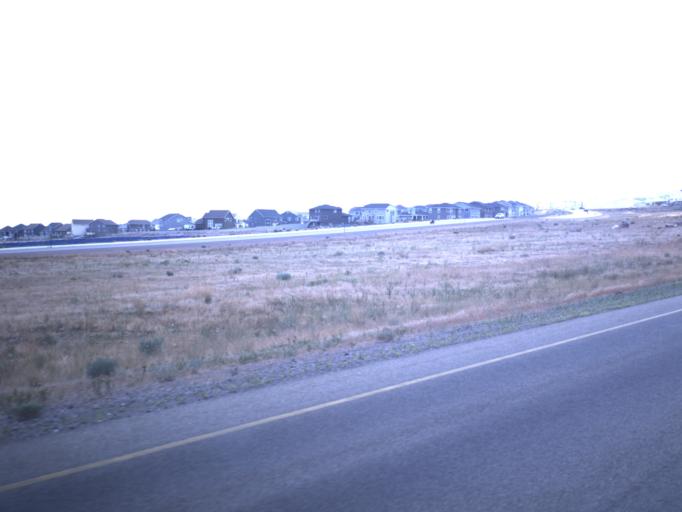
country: US
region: Utah
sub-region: Salt Lake County
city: Herriman
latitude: 40.4953
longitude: -112.0048
